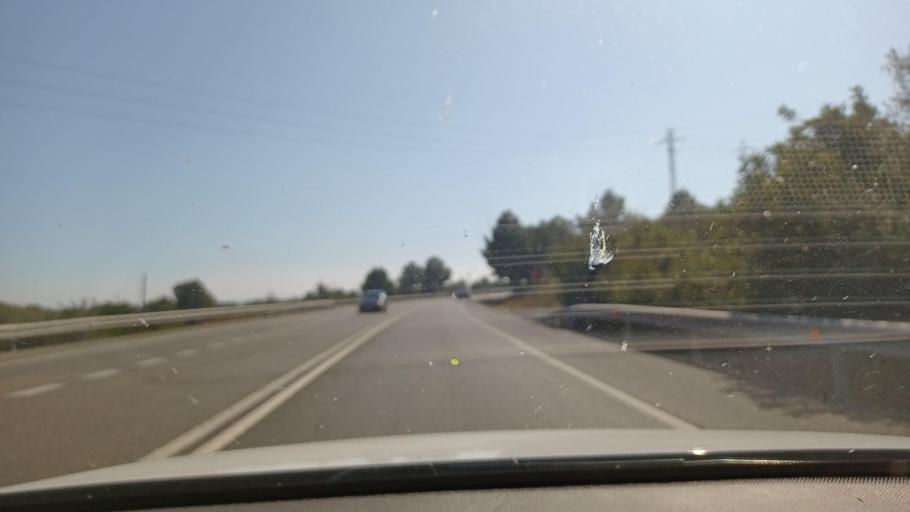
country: ES
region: Catalonia
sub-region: Provincia de Tarragona
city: L'Ampolla
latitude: 40.8421
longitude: 0.7106
